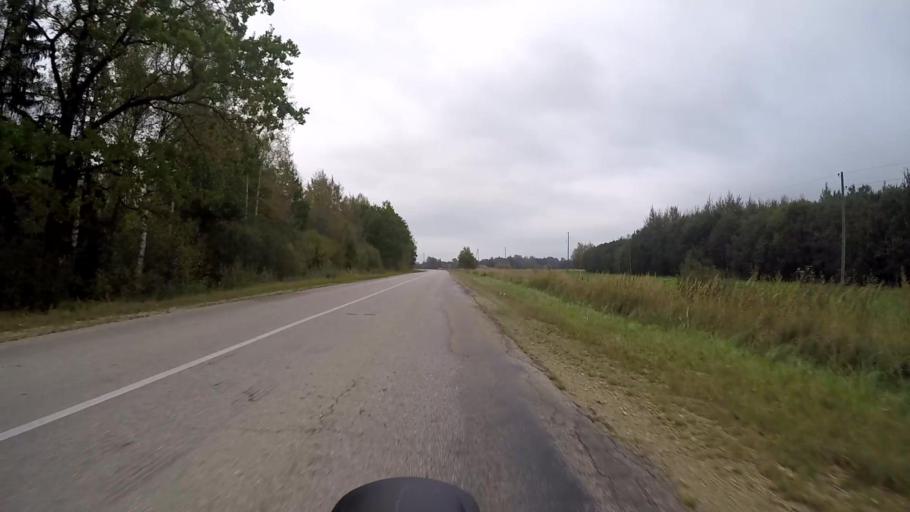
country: LV
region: Saulkrastu
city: Saulkrasti
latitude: 57.2751
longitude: 24.5502
